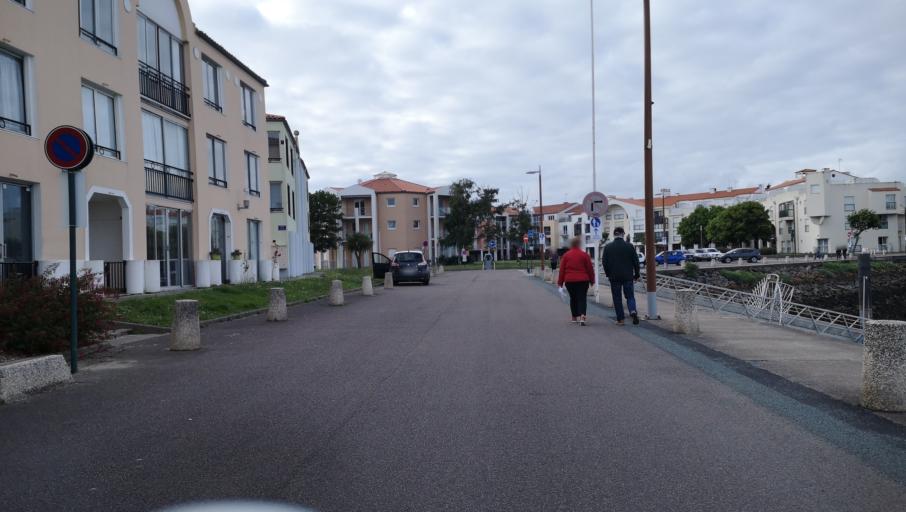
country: FR
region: Pays de la Loire
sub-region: Departement de la Vendee
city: Les Sables-d'Olonne
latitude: 46.5013
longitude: -1.7958
